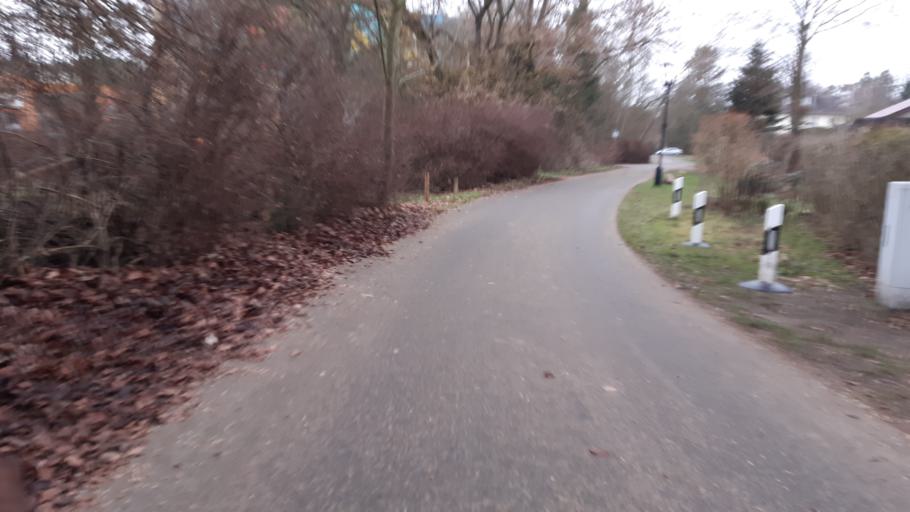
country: DE
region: Brandenburg
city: Templin
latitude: 53.1113
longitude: 13.5330
